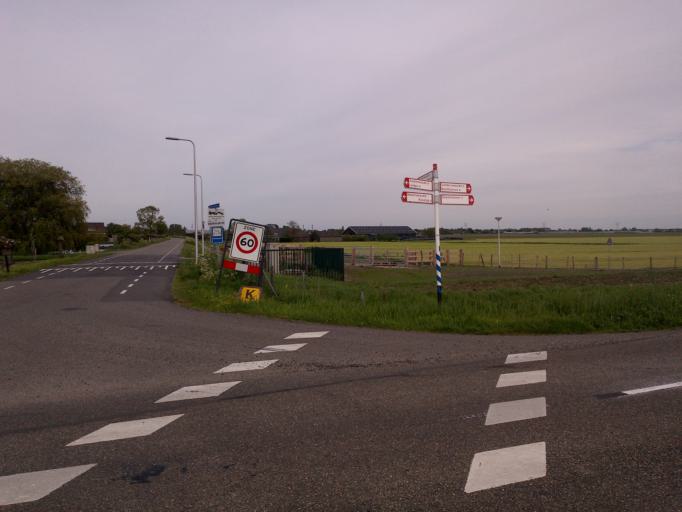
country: NL
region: South Holland
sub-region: Gemeente Rijnwoude
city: Benthuizen
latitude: 52.1049
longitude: 4.5362
